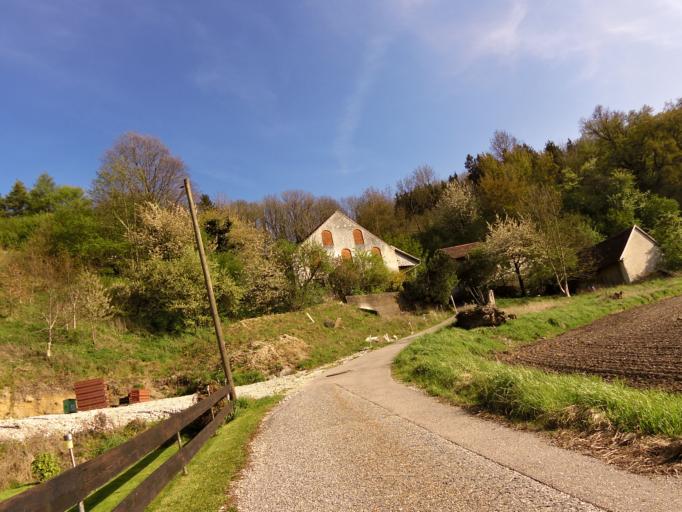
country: DE
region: Bavaria
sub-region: Lower Bavaria
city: Eching
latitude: 48.4907
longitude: 12.0344
